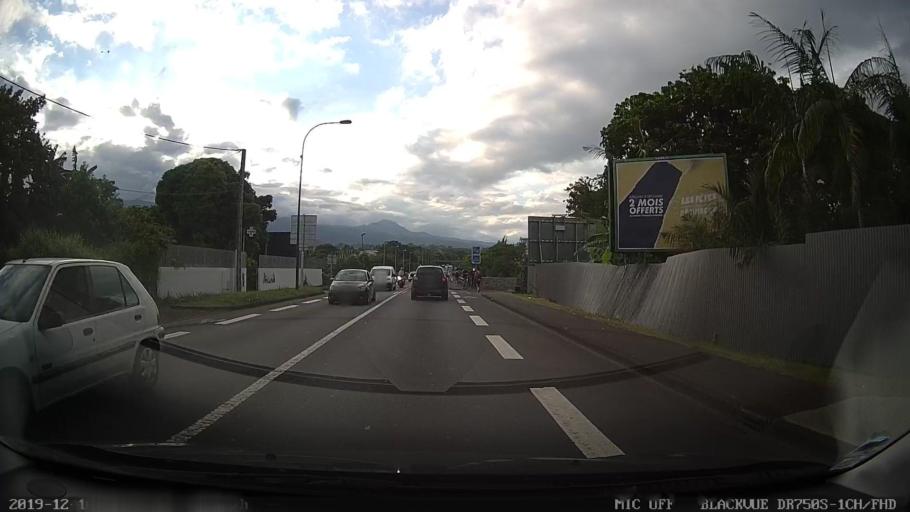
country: RE
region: Reunion
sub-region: Reunion
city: Saint-Benoit
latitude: -21.0413
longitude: 55.7135
